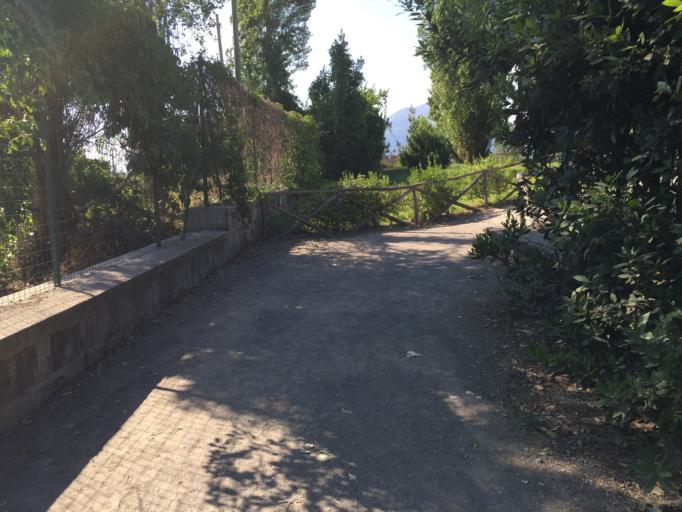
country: IT
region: Campania
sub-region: Provincia di Napoli
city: Torre Annunziata
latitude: 40.7530
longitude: 14.4780
